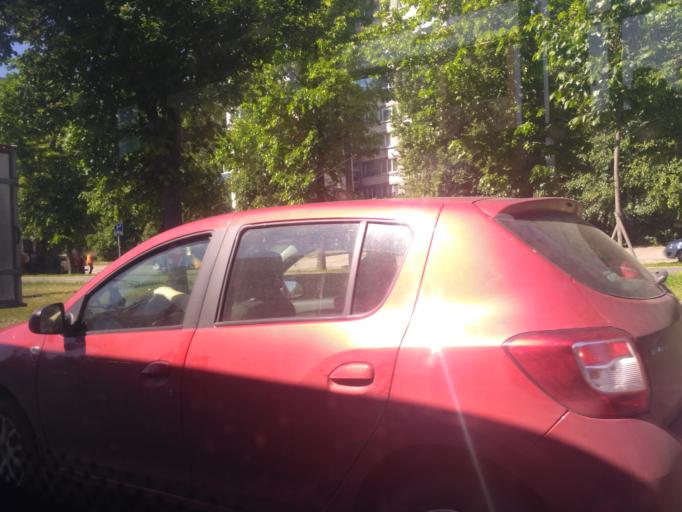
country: RU
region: Leningrad
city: Kalininskiy
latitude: 59.9716
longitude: 30.4120
